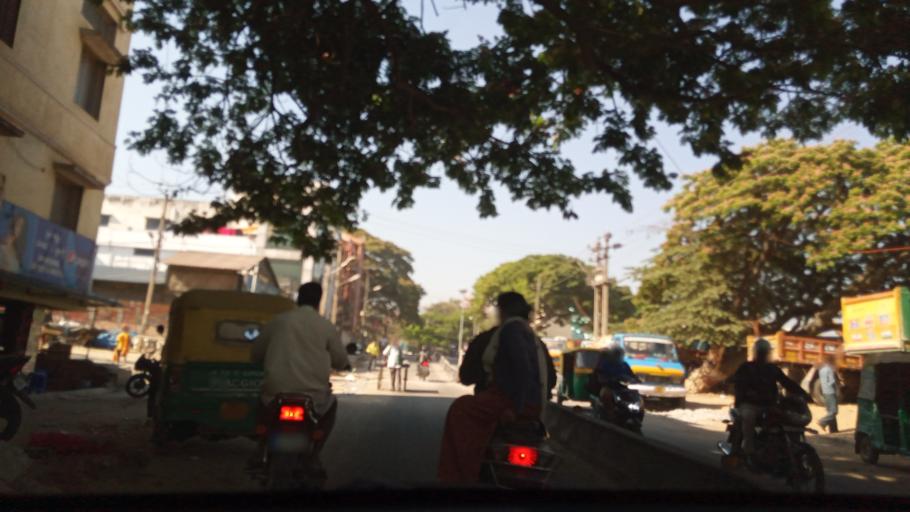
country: IN
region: Karnataka
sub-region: Bangalore Urban
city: Bangalore
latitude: 13.0198
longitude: 77.5403
